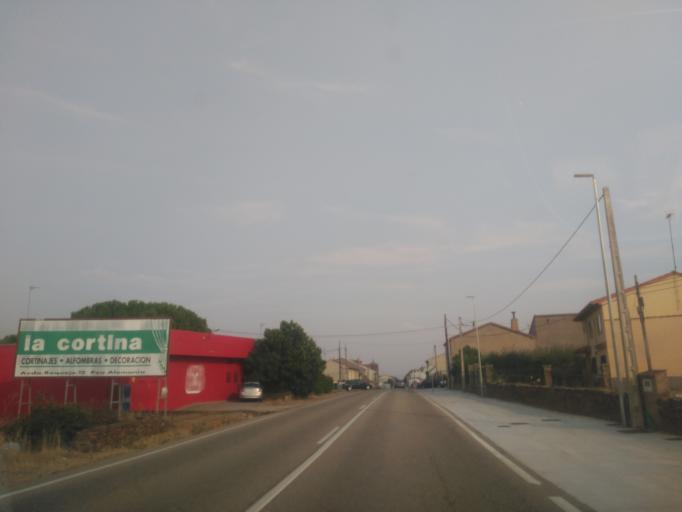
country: ES
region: Castille and Leon
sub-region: Provincia de Zamora
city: Tabara
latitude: 41.8298
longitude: -5.9636
